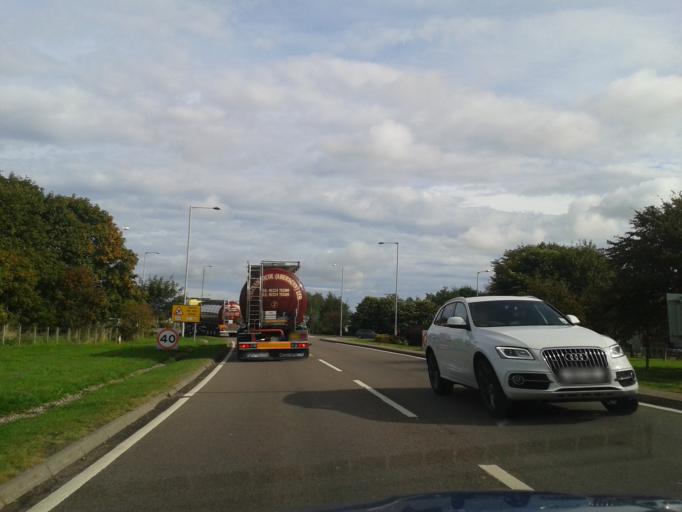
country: GB
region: Scotland
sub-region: Moray
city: Forres
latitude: 57.6071
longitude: -3.6313
